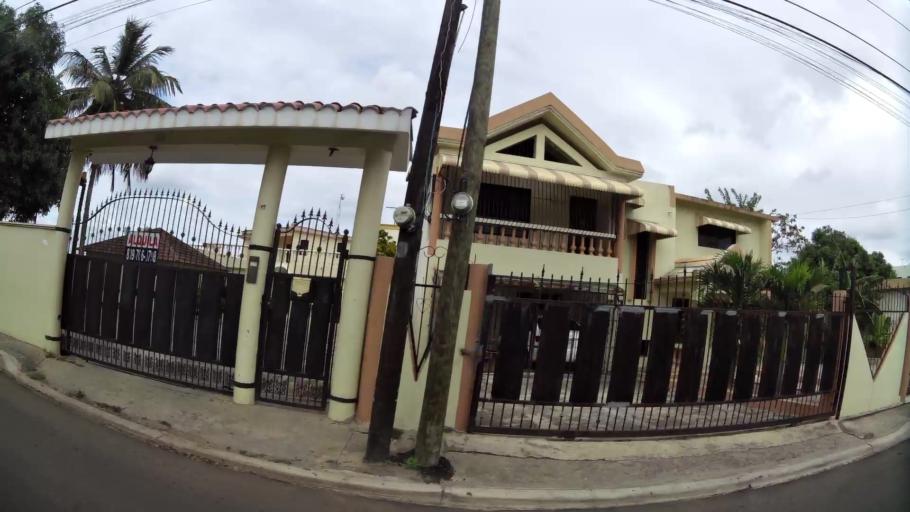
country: DO
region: Santiago
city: Santiago de los Caballeros
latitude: 19.4359
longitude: -70.6709
